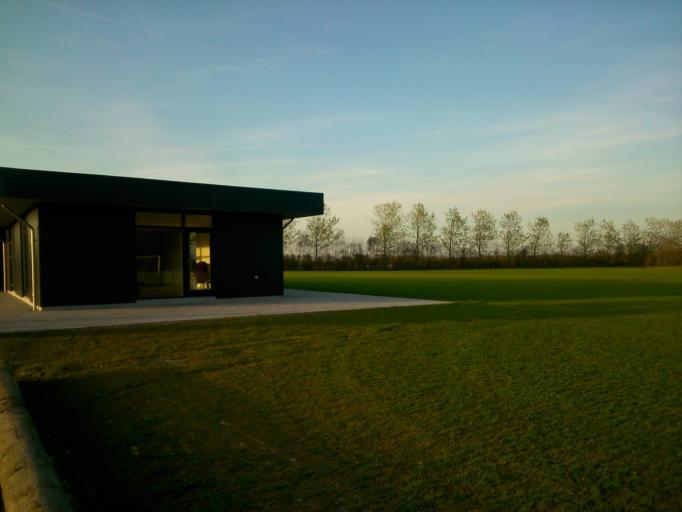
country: DK
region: Central Jutland
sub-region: Ringkobing-Skjern Kommune
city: Skjern
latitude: 55.8909
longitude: 8.4168
